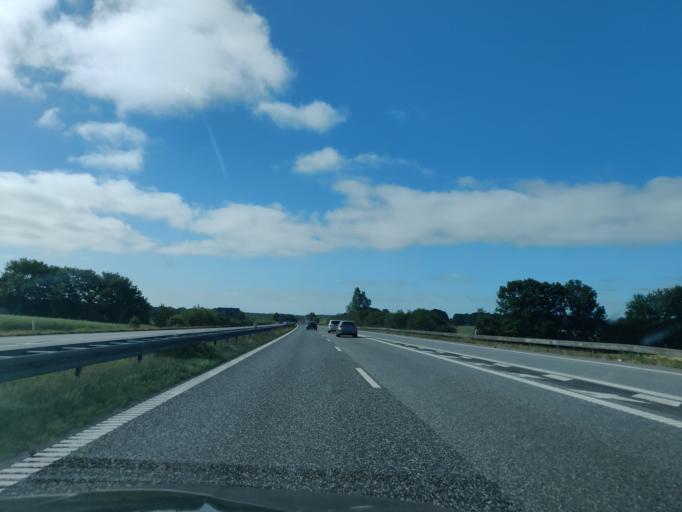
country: DK
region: North Denmark
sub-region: Mariagerfjord Kommune
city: Hobro
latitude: 56.6641
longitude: 9.7344
